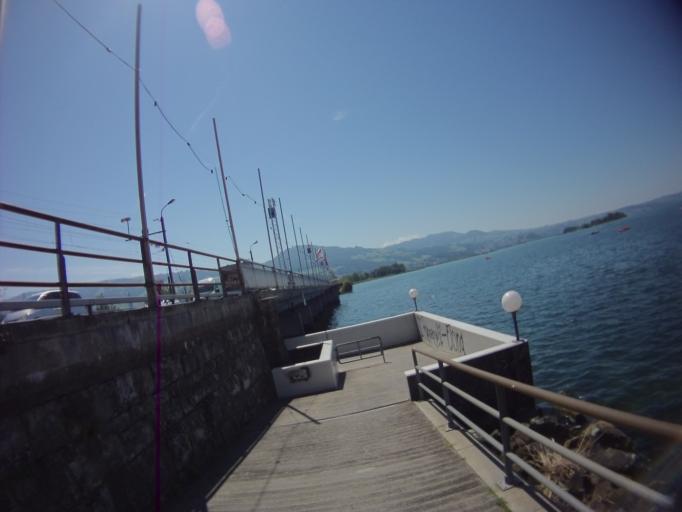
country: CH
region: Saint Gallen
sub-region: Wahlkreis See-Gaster
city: Rapperswil
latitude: 47.2239
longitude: 8.8134
